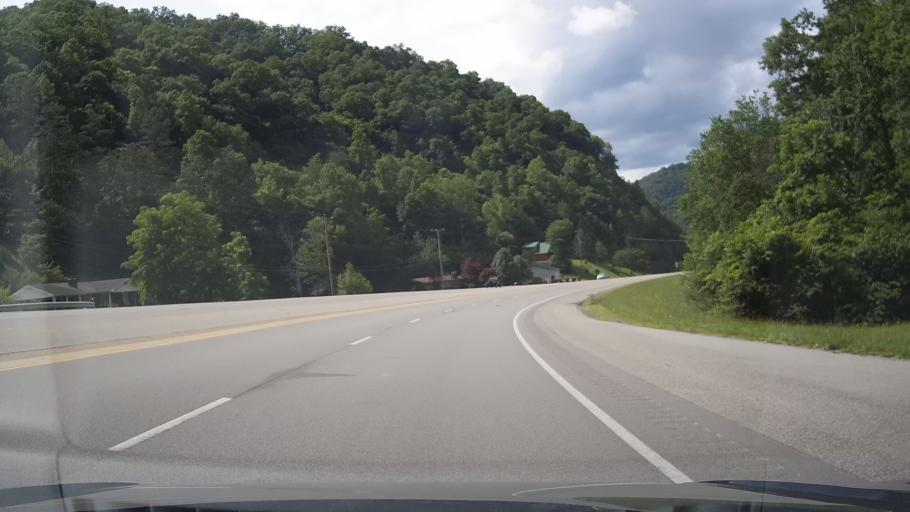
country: US
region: Kentucky
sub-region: Letcher County
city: Jenkins
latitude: 37.3104
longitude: -82.5479
